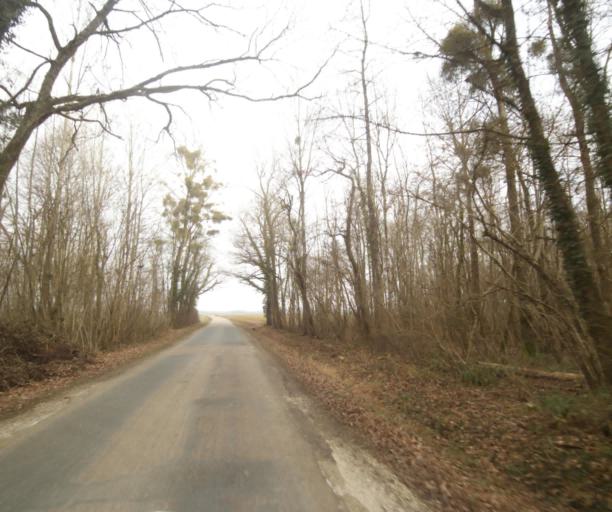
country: FR
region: Champagne-Ardenne
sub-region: Departement de la Haute-Marne
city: Villiers-en-Lieu
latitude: 48.6675
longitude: 4.8347
